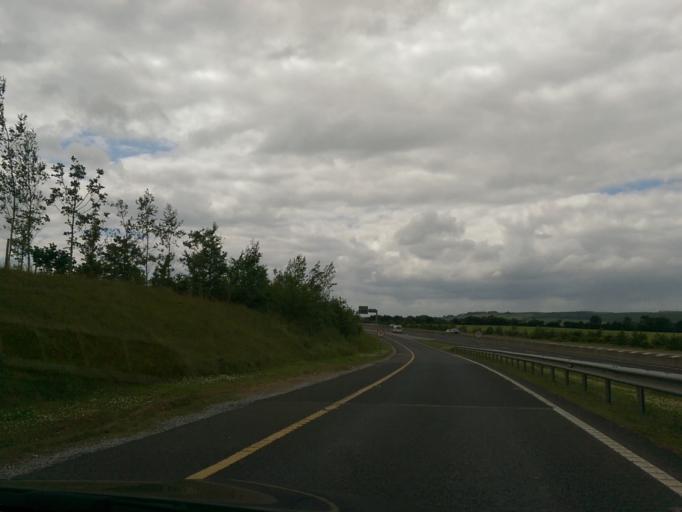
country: IE
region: Munster
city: Thurles
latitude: 52.6219
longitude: -7.7756
